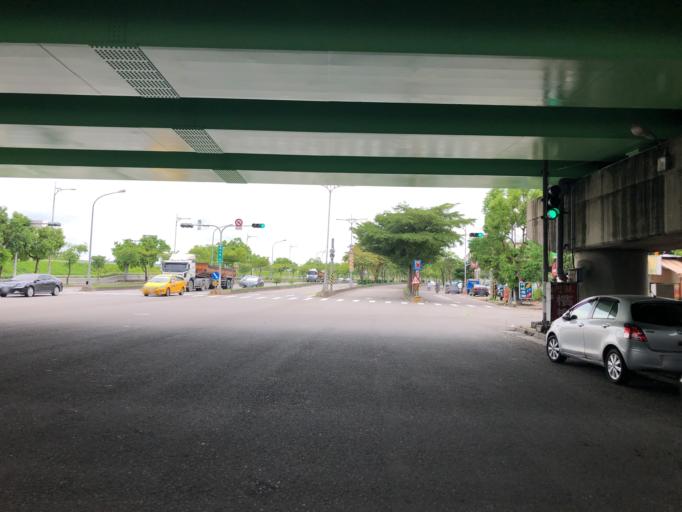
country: TW
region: Taiwan
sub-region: Taichung City
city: Taichung
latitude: 24.0831
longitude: 120.6642
